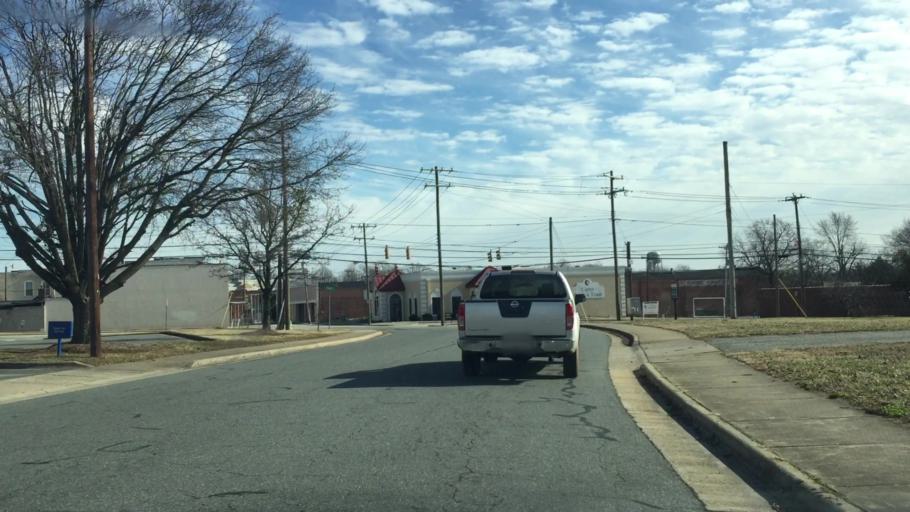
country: US
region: North Carolina
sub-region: Rockingham County
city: Reidsville
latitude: 36.3591
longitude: -79.6666
